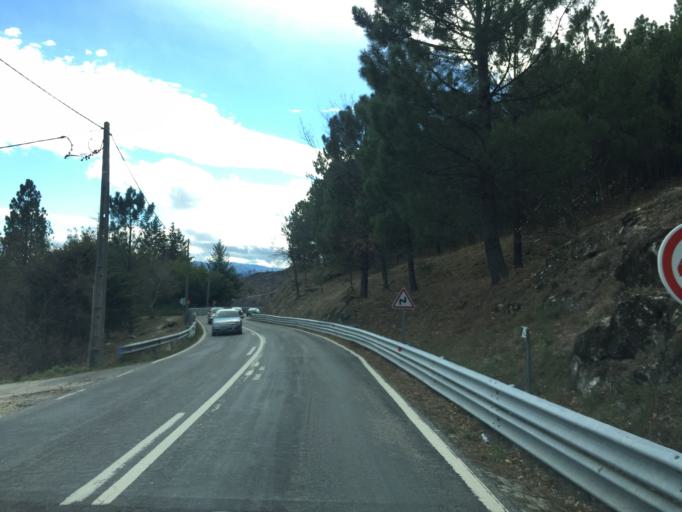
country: PT
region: Castelo Branco
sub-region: Covilha
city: Covilha
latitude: 40.2839
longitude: -7.5204
